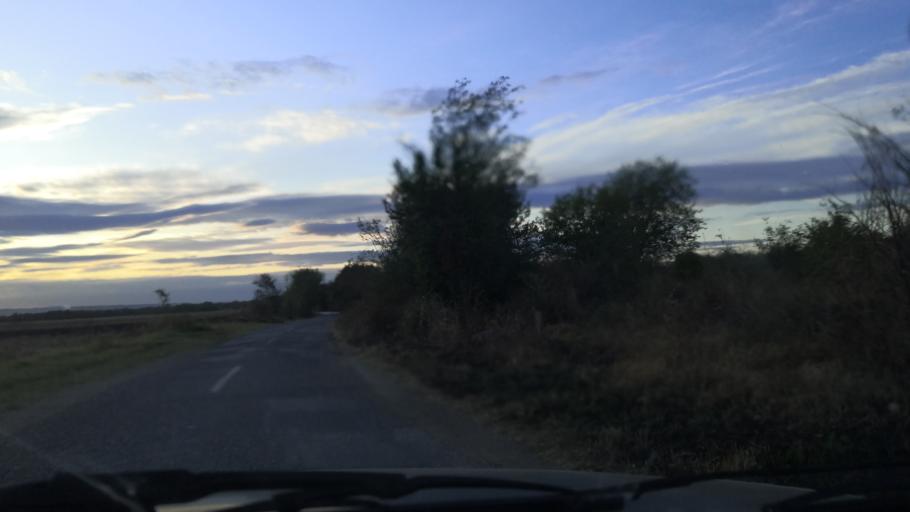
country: RO
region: Mehedinti
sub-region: Comuna Gruia
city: Izvoarele
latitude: 44.2769
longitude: 22.6566
